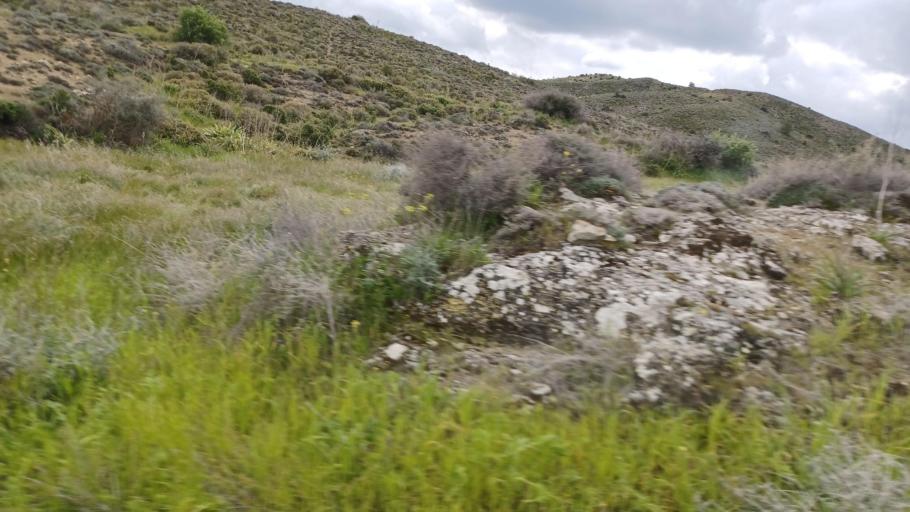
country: CY
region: Lefkosia
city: Lefka
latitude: 35.0881
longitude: 32.9346
